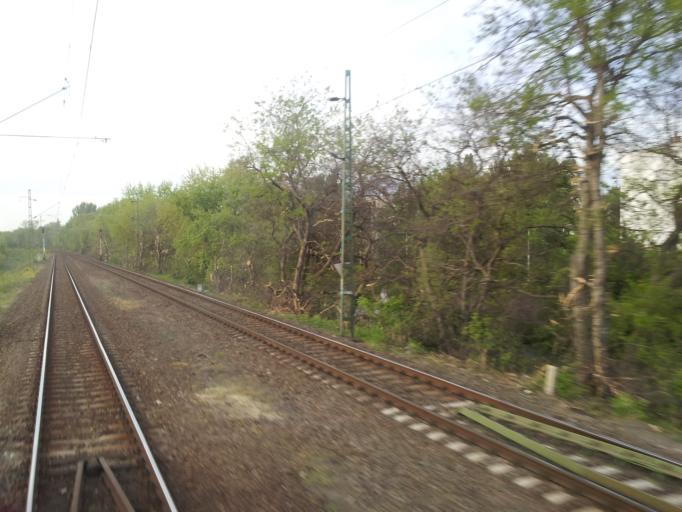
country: HU
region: Budapest
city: Budapest XVI. keruelet
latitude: 47.5057
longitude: 19.1565
